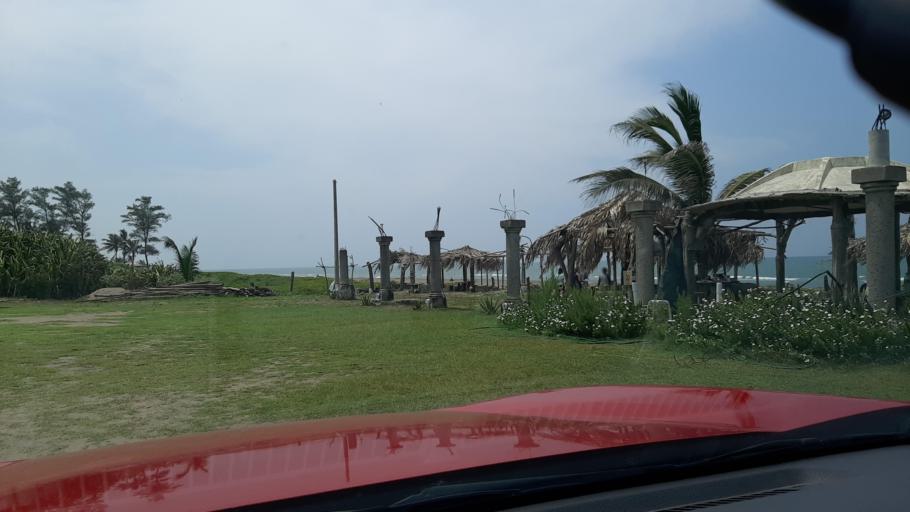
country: MX
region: Veracruz
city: Nautla
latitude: 20.2608
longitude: -96.8030
